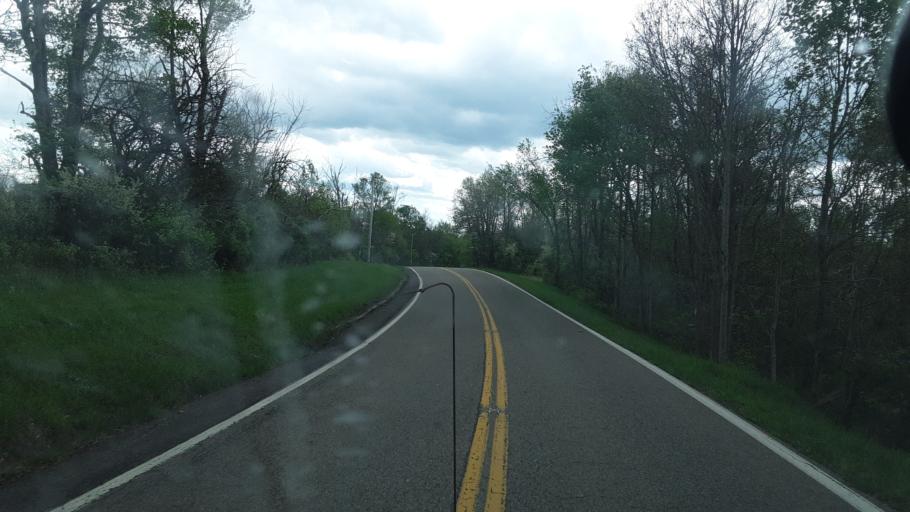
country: US
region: Ohio
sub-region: Noble County
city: Caldwell
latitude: 39.7455
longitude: -81.6358
